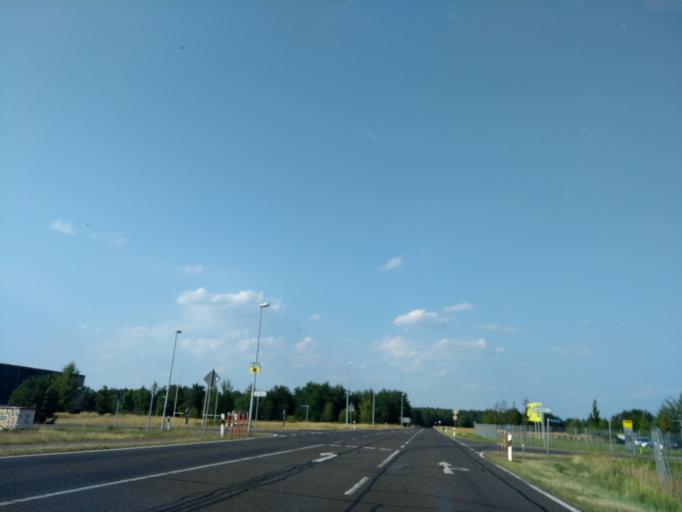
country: DE
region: Brandenburg
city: Lubbenau
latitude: 51.8320
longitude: 13.9161
